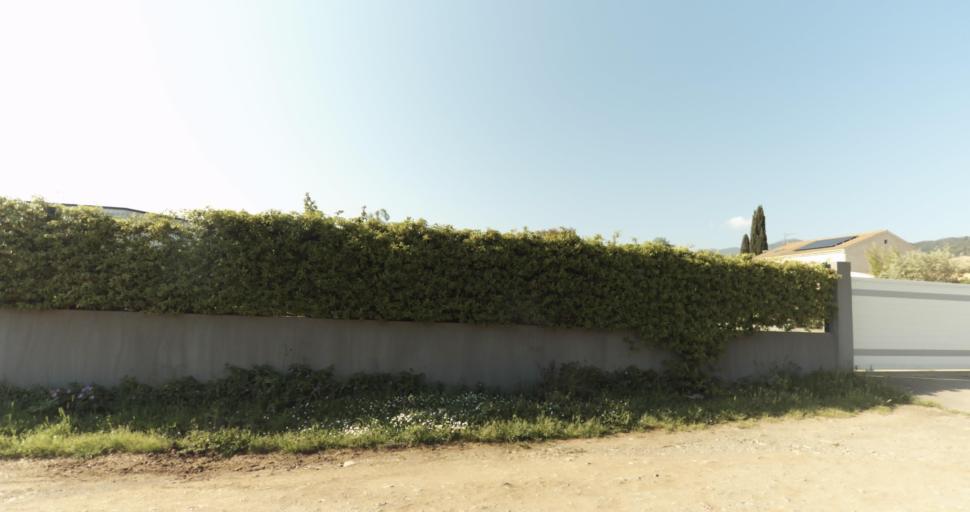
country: FR
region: Corsica
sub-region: Departement de la Haute-Corse
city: Biguglia
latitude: 42.6329
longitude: 9.4319
